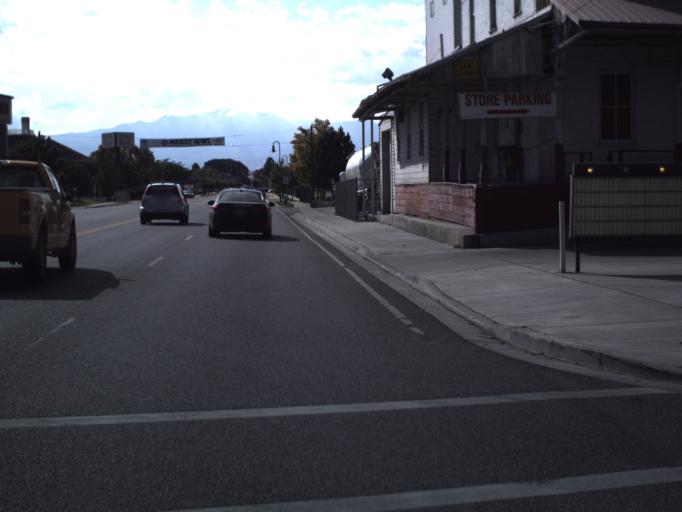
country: US
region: Utah
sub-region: Utah County
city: Lehi
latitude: 40.3883
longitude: -111.8358
